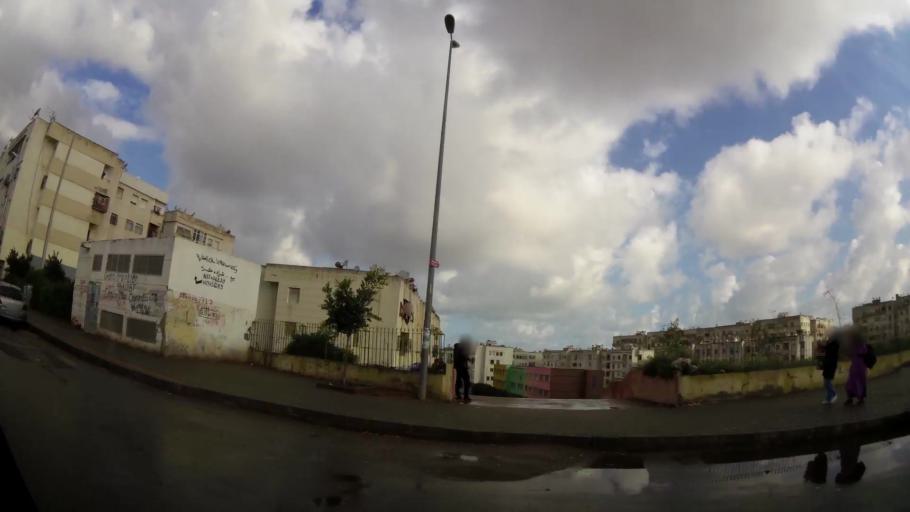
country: MA
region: Grand Casablanca
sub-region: Mediouna
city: Tit Mellil
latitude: 33.5929
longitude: -7.5349
